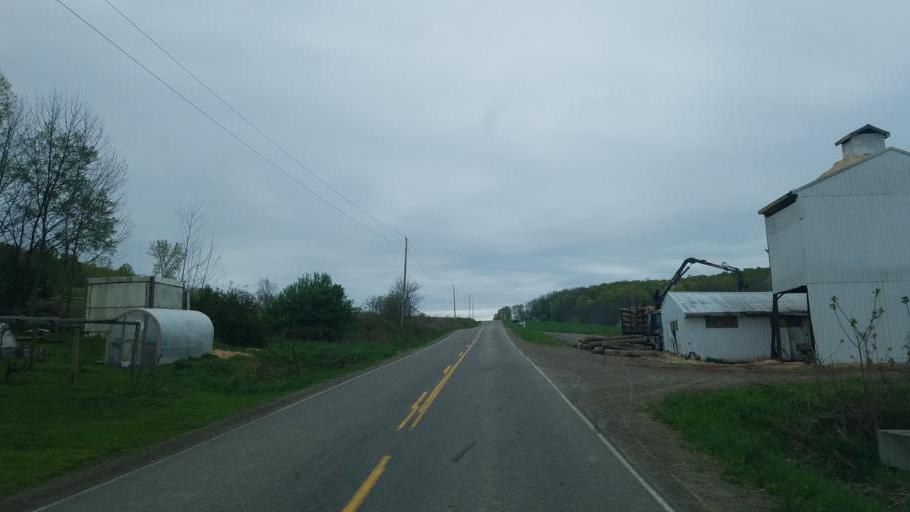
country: US
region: Pennsylvania
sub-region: Tioga County
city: Westfield
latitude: 42.0444
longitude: -77.4664
